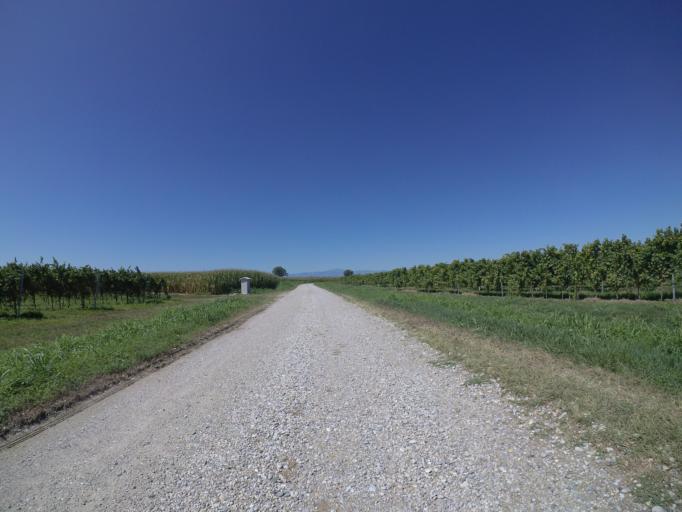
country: IT
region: Friuli Venezia Giulia
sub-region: Provincia di Udine
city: Varmo
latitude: 45.8655
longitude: 13.0108
